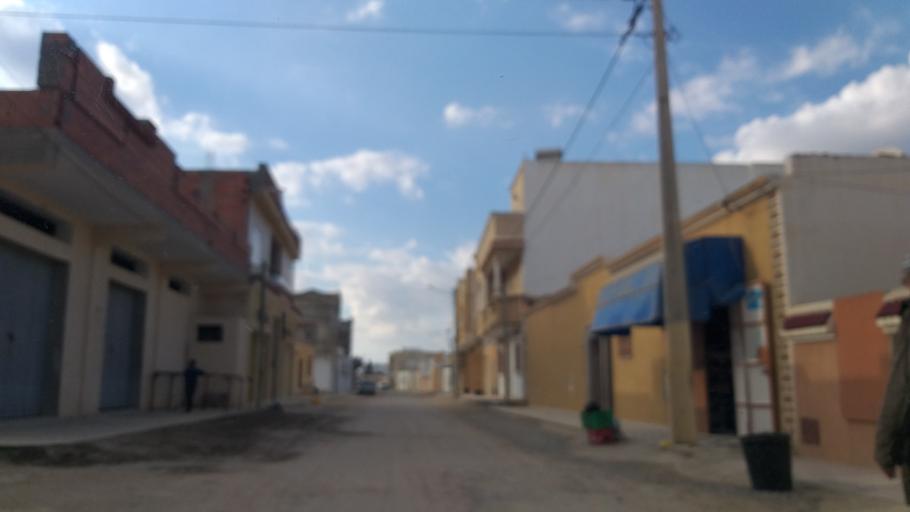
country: TN
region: Al Mahdiyah
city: El Jem
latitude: 35.3048
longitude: 10.7012
